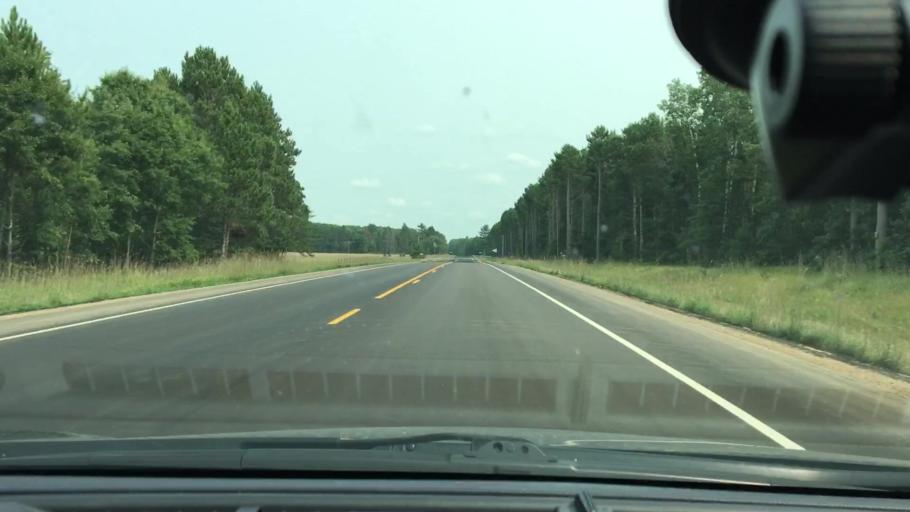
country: US
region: Minnesota
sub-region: Crow Wing County
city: Nisswa
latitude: 46.5292
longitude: -94.2545
